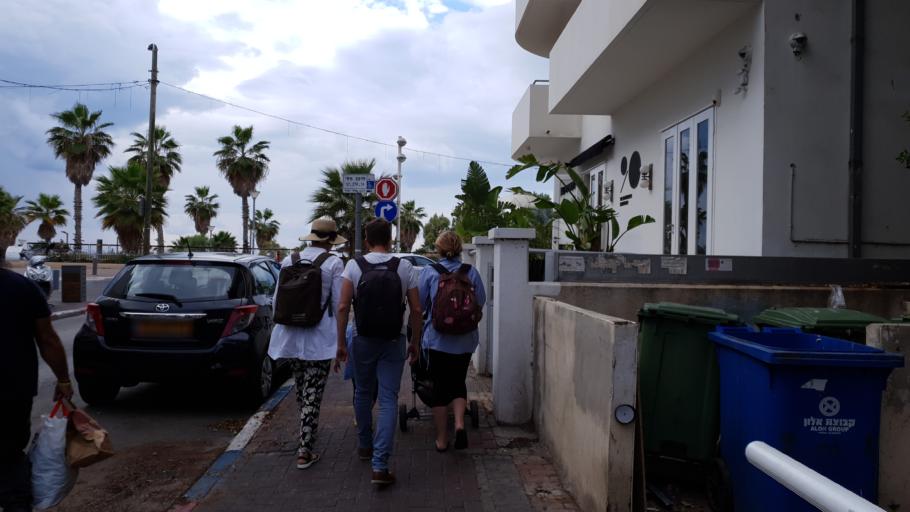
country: IL
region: Tel Aviv
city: Tel Aviv
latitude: 32.0779
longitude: 34.7677
